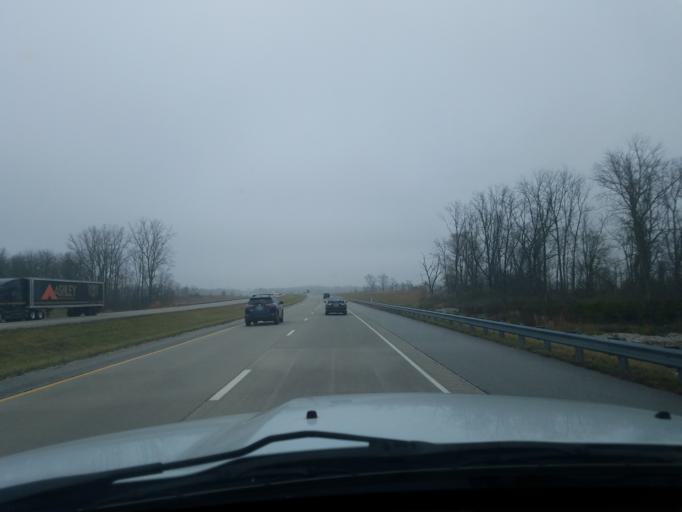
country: US
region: Indiana
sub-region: Howard County
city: Indian Heights
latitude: 40.4272
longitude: -86.0848
